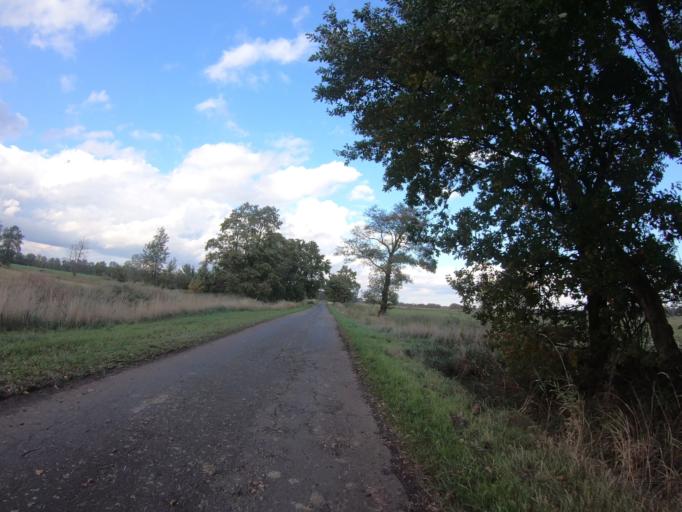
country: DE
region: Lower Saxony
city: Wagenhoff
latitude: 52.5367
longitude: 10.5505
